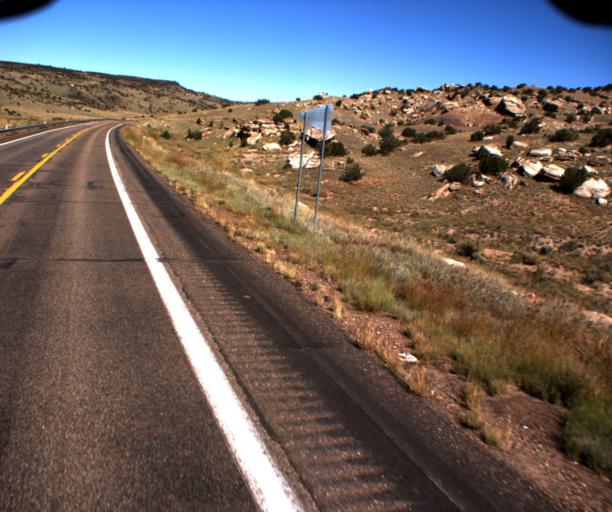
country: US
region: Arizona
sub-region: Apache County
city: Saint Johns
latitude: 34.3312
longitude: -109.3872
